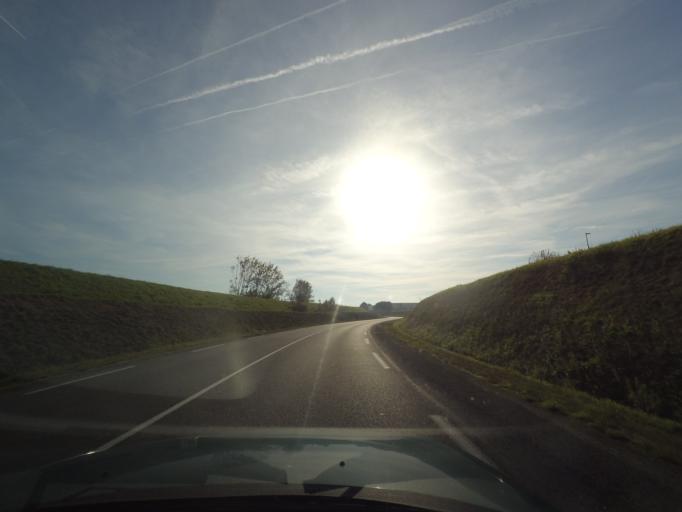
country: FR
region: Pays de la Loire
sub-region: Departement de la Vendee
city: Montaigu
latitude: 46.9649
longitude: -1.3038
